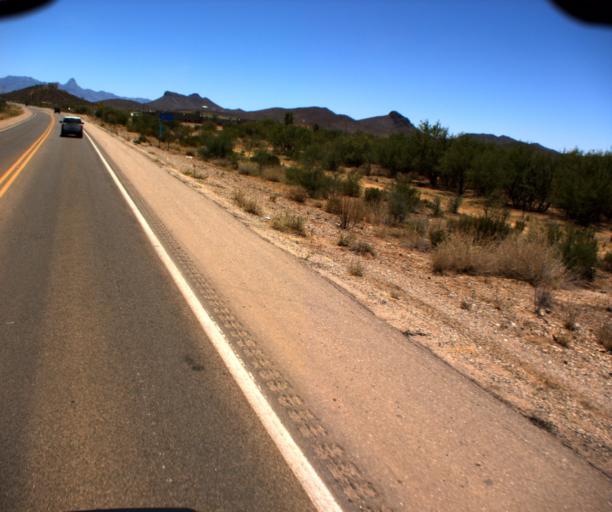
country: US
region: Arizona
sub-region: Pima County
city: Sells
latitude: 31.9241
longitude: -111.8970
